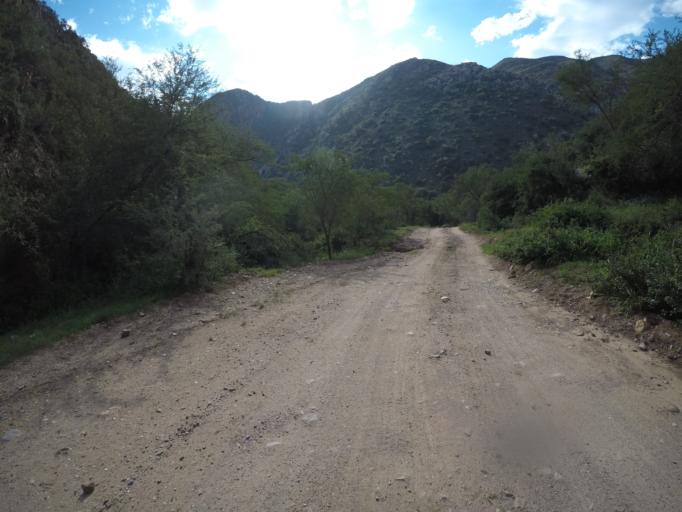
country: ZA
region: Eastern Cape
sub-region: Cacadu District Municipality
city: Kareedouw
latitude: -33.6374
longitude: 24.3216
